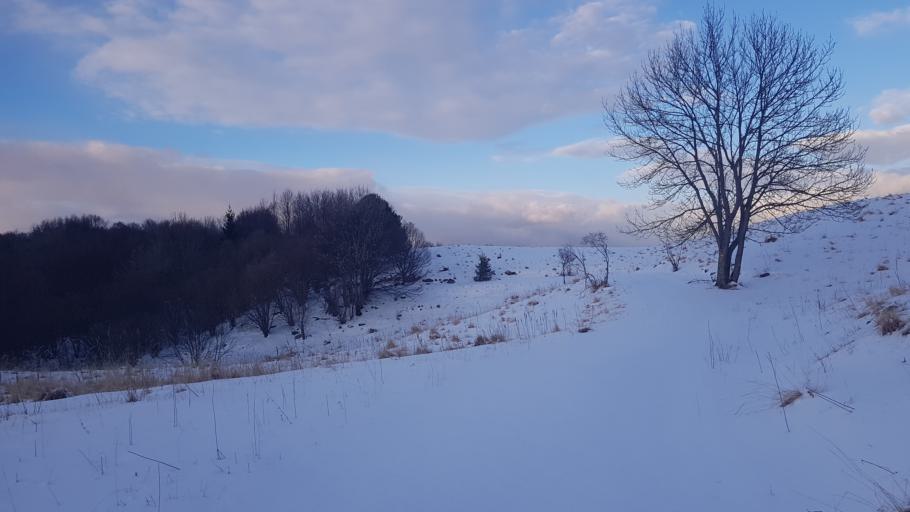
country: IT
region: Friuli Venezia Giulia
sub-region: Provincia di Udine
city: Torreano
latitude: 46.1853
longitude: 13.4162
